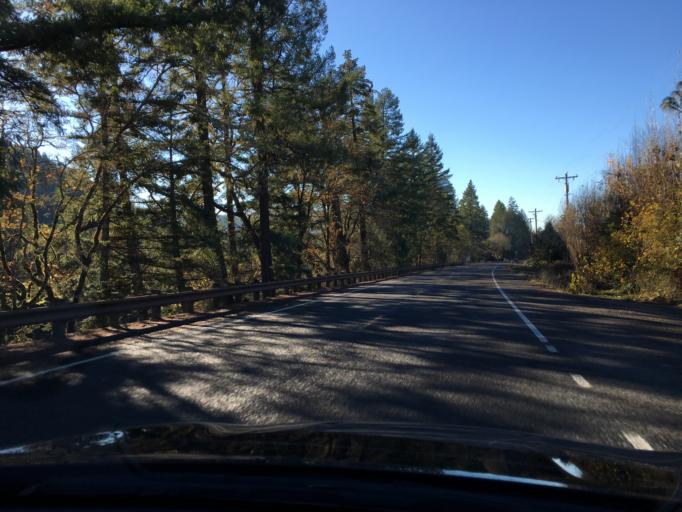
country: US
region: Oregon
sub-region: Douglas County
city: Glide
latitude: 43.3228
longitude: -123.0294
